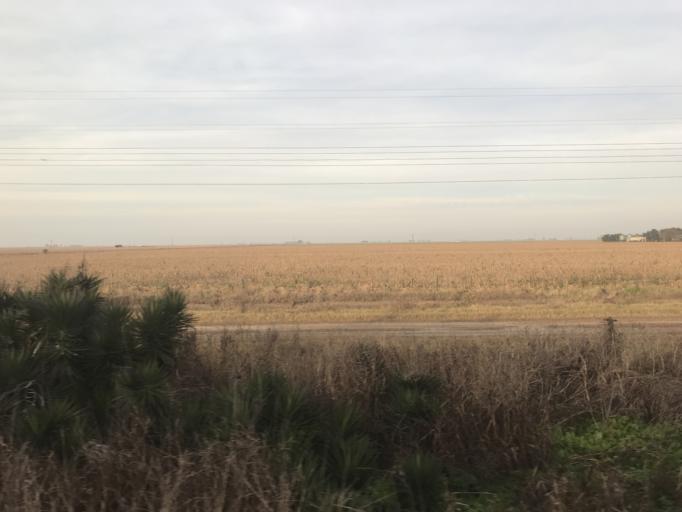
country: AR
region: Cordoba
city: Marcos Juarez
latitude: -32.6867
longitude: -62.1754
